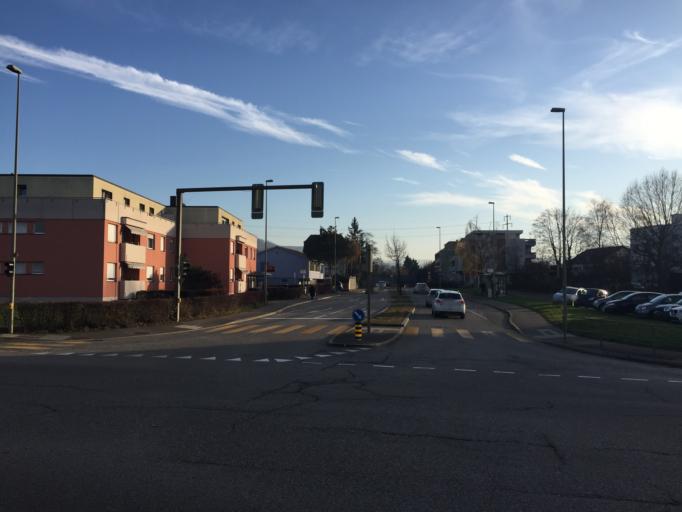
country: CH
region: Aargau
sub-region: Bezirk Rheinfelden
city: Kaiseraugst
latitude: 47.5352
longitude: 7.7127
